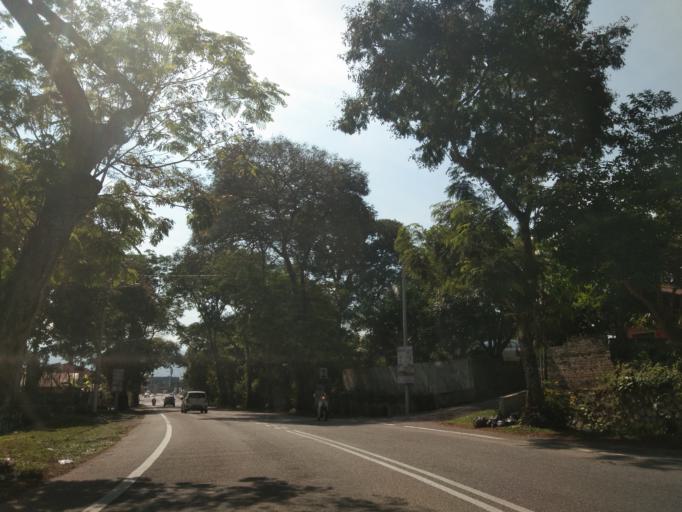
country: MY
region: Perak
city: Ipoh
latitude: 4.5713
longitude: 101.1096
